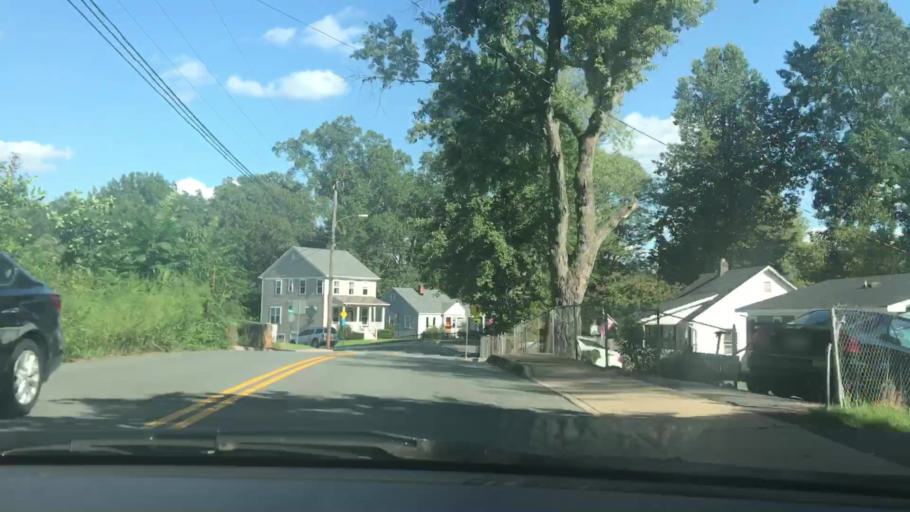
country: US
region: Virginia
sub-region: City of Charlottesville
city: Charlottesville
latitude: 38.0262
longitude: -78.5083
